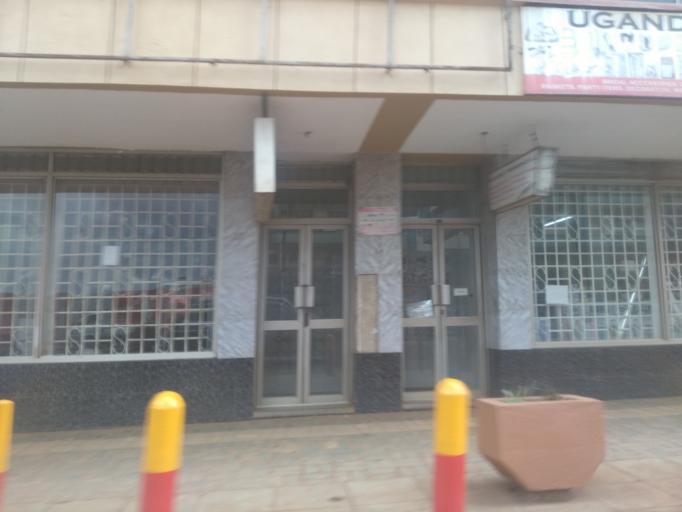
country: UG
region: Central Region
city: Kampala Central Division
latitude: 0.3201
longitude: 32.5741
